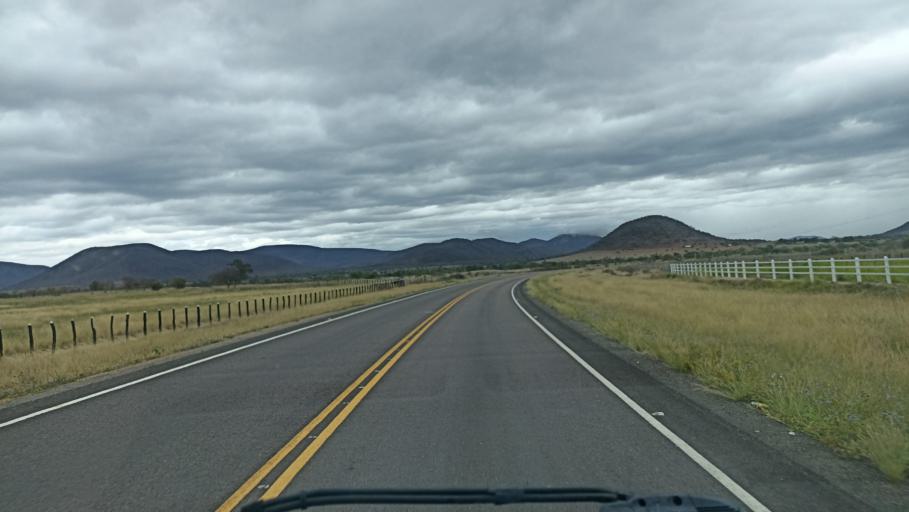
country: BR
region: Bahia
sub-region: Iacu
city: Iacu
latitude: -12.9216
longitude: -40.4150
